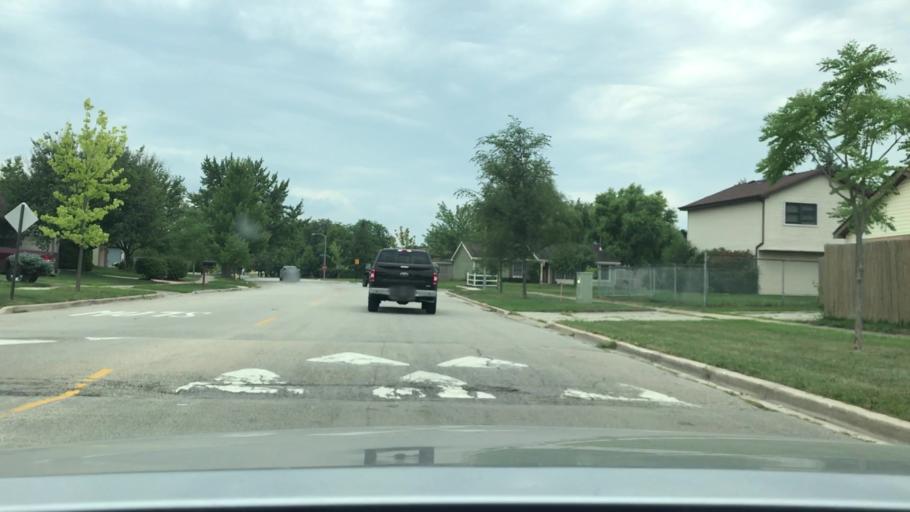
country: US
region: Illinois
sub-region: Will County
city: Bolingbrook
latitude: 41.7055
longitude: -88.0392
